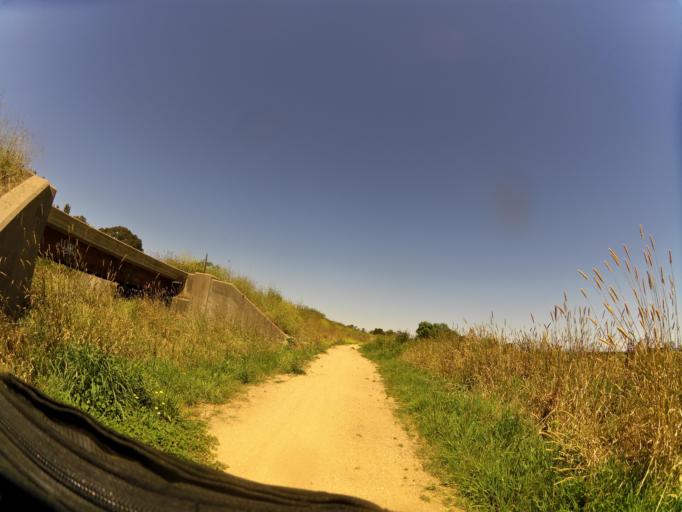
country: AU
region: Victoria
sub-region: Wellington
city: Sale
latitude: -37.9806
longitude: 147.0694
